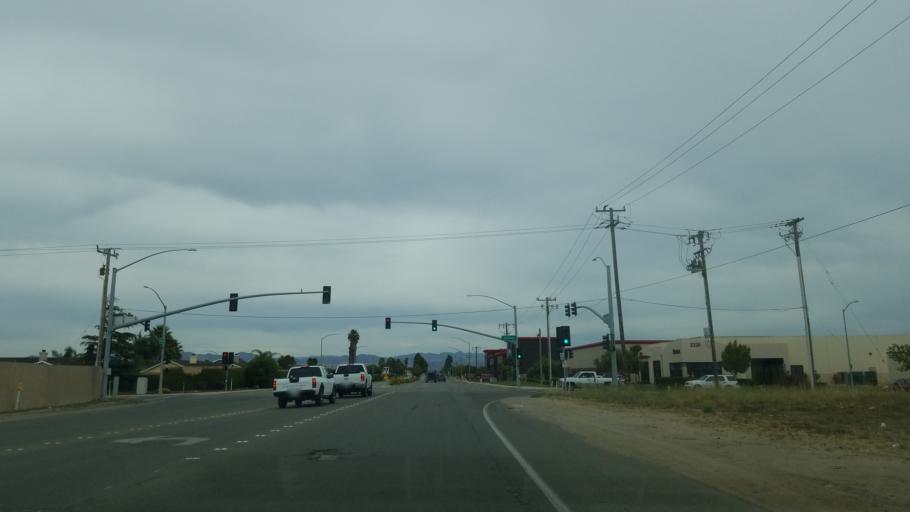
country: US
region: California
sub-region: Santa Barbara County
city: Santa Maria
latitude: 34.9208
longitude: -120.4649
